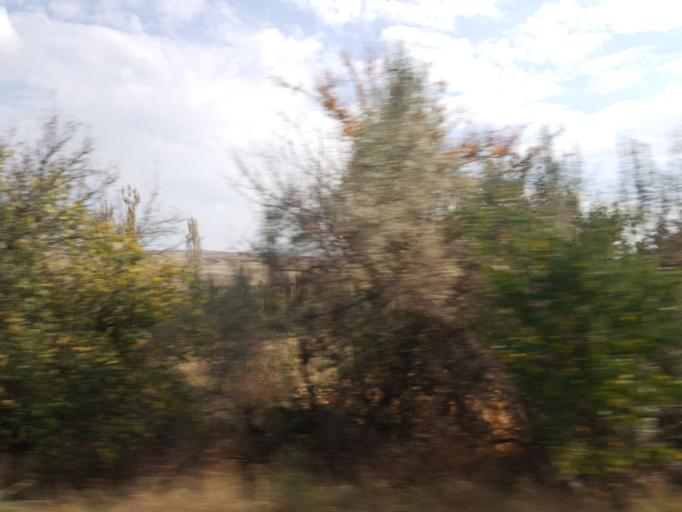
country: TR
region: Corum
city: Sungurlu
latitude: 40.2153
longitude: 34.5540
